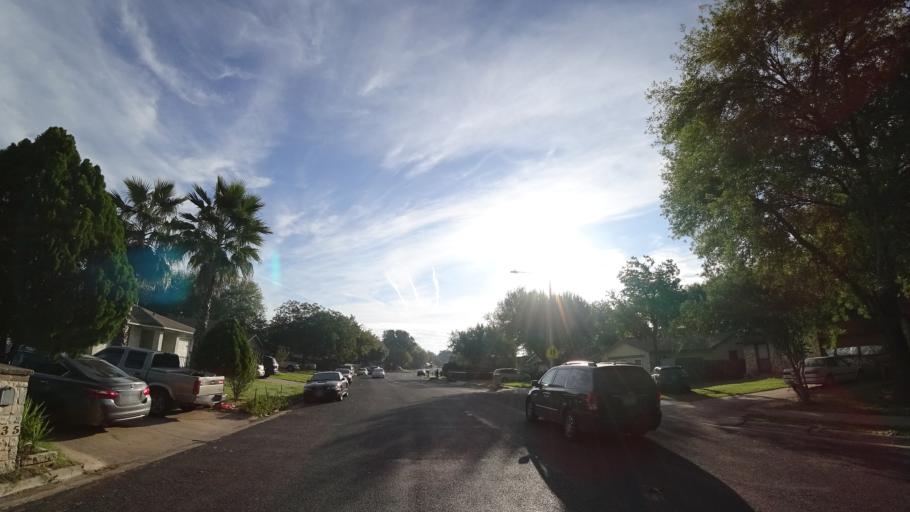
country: US
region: Texas
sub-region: Travis County
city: Onion Creek
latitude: 30.1909
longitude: -97.7459
